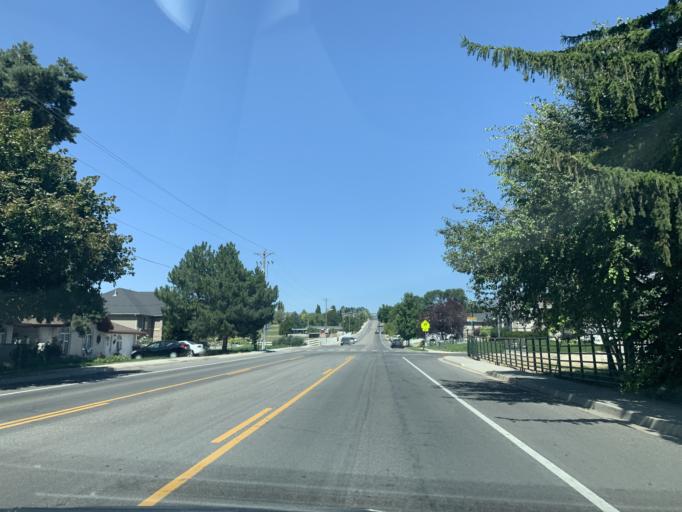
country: US
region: Utah
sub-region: Utah County
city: Lehi
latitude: 40.4003
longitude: -111.8302
